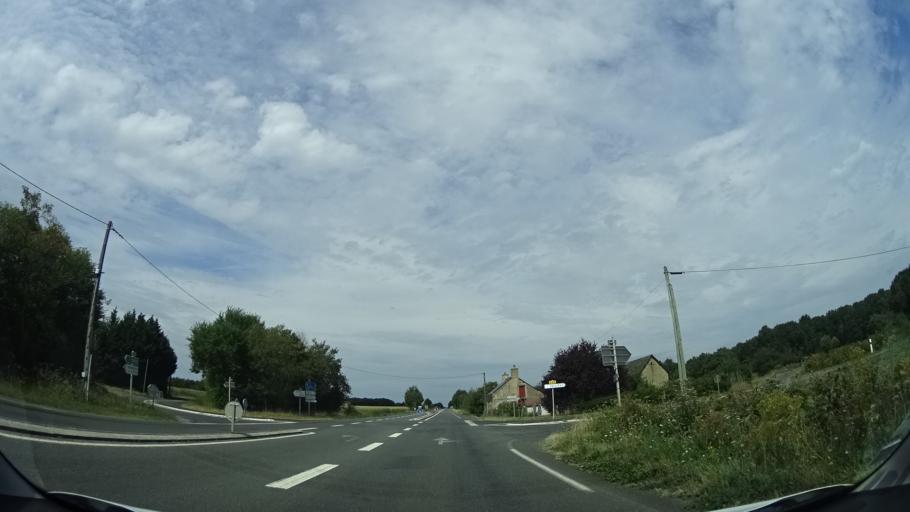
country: FR
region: Pays de la Loire
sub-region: Departement de la Sarthe
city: Vion
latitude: 47.7644
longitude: -0.1894
